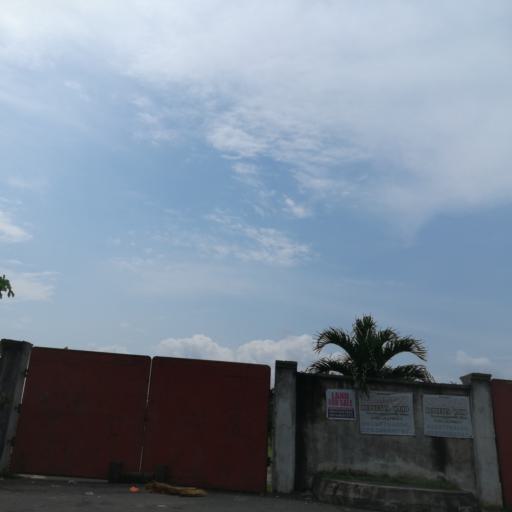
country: NG
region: Rivers
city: Port Harcourt
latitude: 4.8404
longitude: 7.0146
